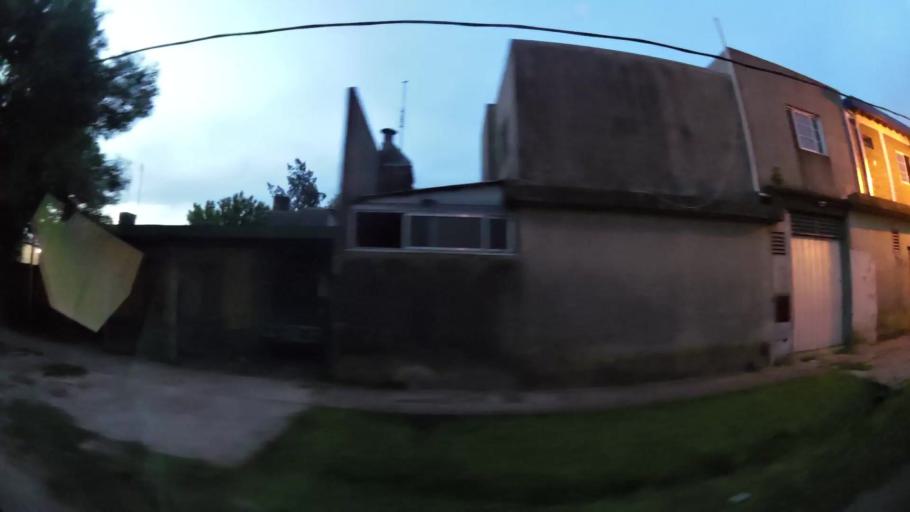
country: AR
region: Buenos Aires
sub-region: Partido de Quilmes
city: Quilmes
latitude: -34.8036
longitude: -58.2914
